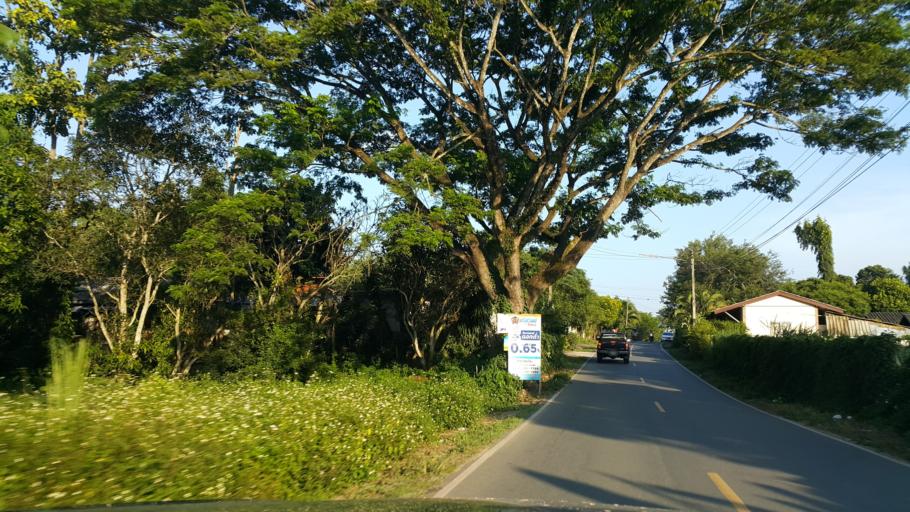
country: TH
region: Chiang Mai
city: San Sai
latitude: 18.9362
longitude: 98.9364
